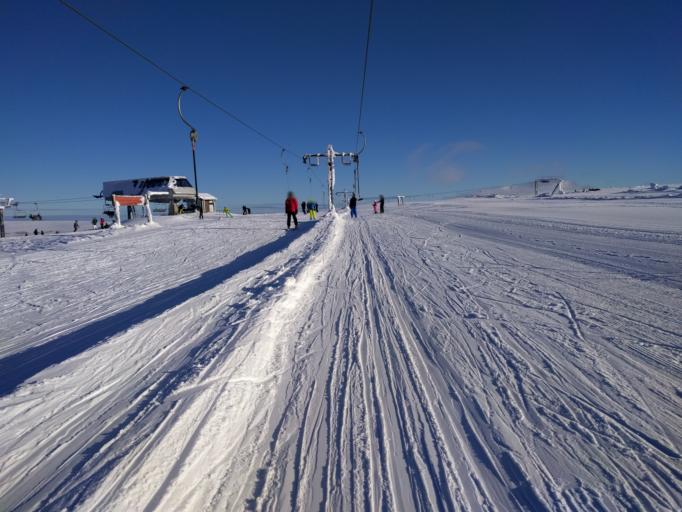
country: NO
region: Hedmark
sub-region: Trysil
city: Innbygda
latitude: 61.1740
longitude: 13.0218
